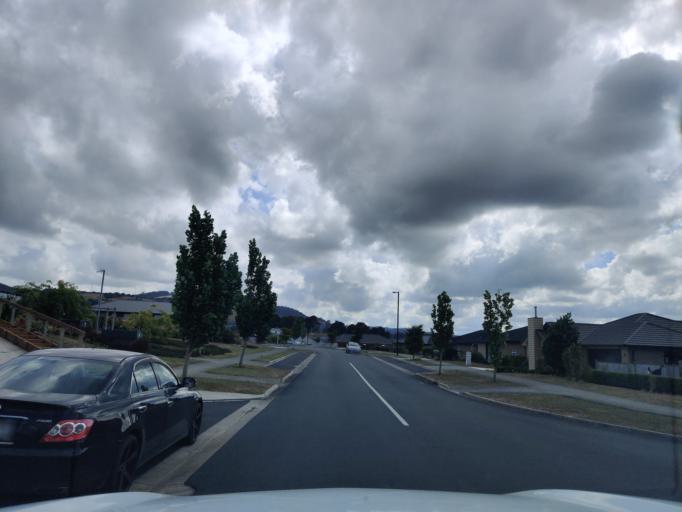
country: NZ
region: Auckland
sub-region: Auckland
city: Pukekohe East
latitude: -37.2385
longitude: 175.0116
